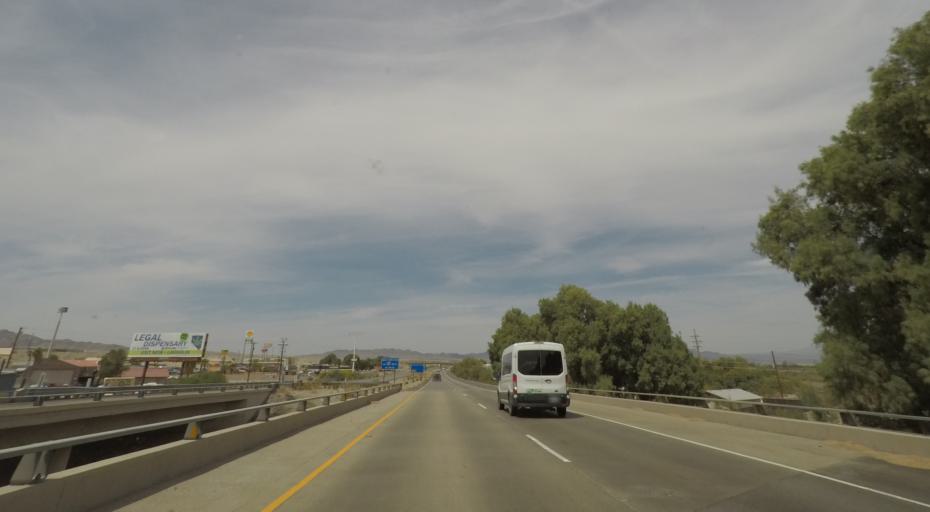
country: US
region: California
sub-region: San Bernardino County
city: Needles
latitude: 34.8498
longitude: -114.6198
